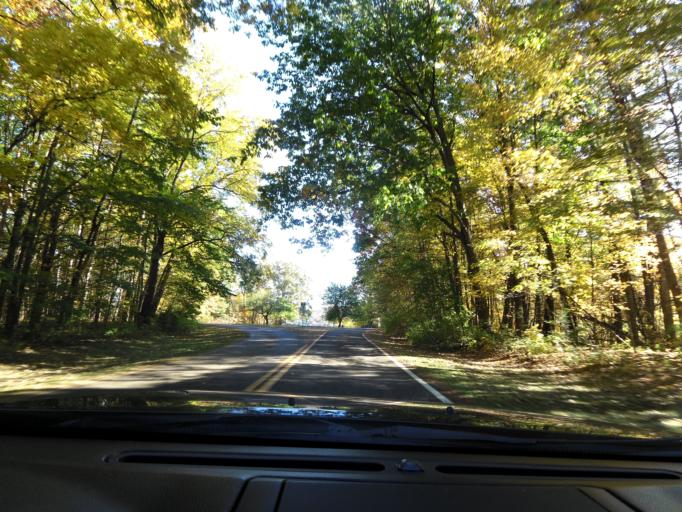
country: US
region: New York
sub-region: Wyoming County
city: Castile
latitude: 42.6398
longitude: -77.9847
